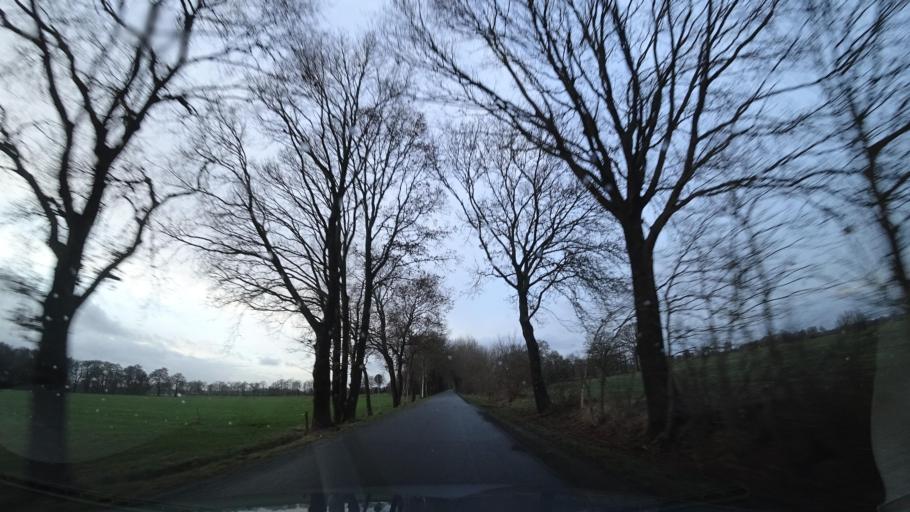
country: DE
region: Lower Saxony
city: Hatten
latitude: 53.0532
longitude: 8.2927
